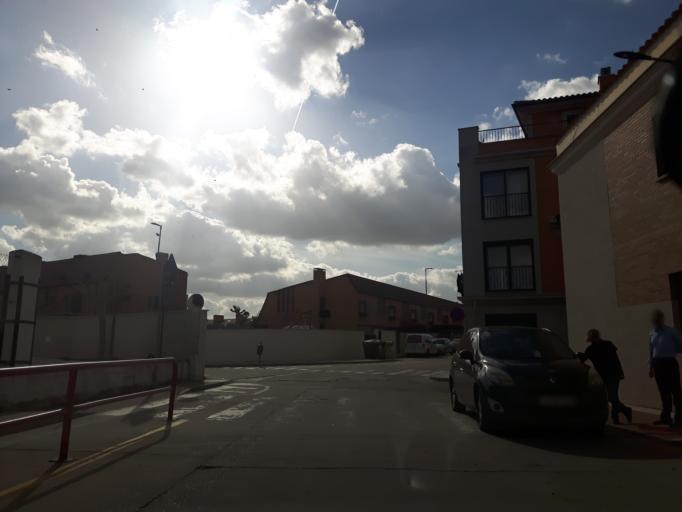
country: ES
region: Castille and Leon
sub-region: Provincia de Salamanca
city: Castellanos de Moriscos
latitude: 41.0173
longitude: -5.5898
